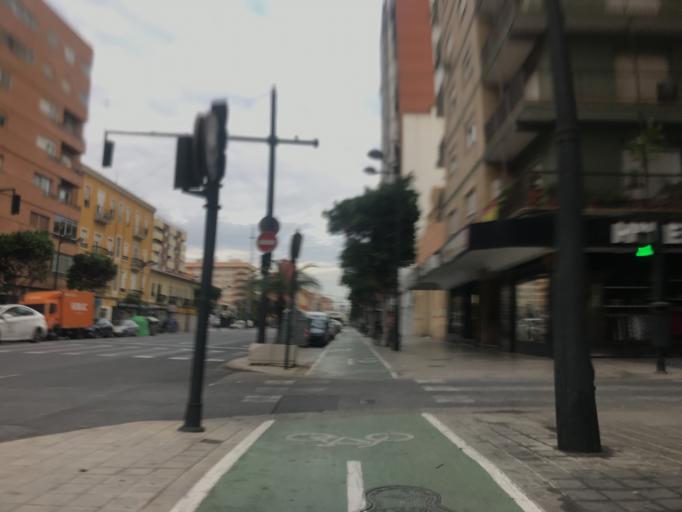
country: ES
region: Valencia
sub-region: Provincia de Valencia
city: Valencia
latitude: 39.4652
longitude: -0.3498
